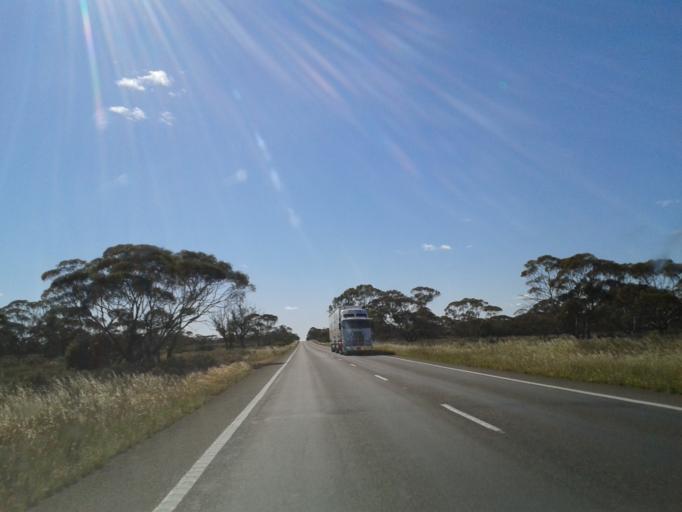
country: AU
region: South Australia
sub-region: Renmark Paringa
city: Renmark
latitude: -34.2744
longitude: 141.0143
